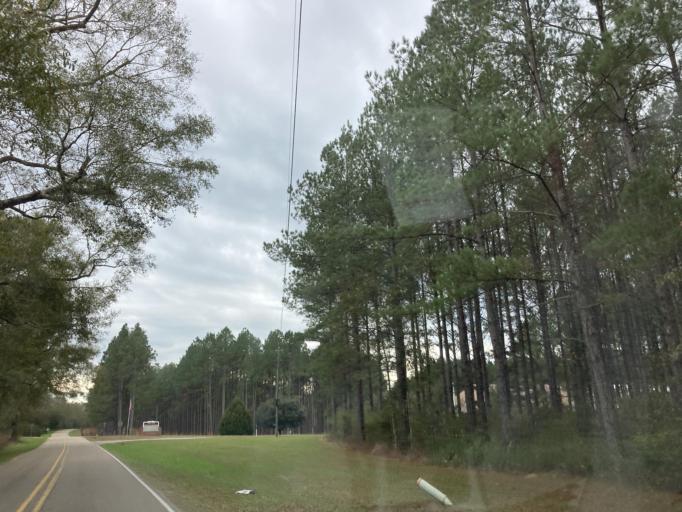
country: US
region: Mississippi
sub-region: Stone County
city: Wiggins
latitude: 30.9632
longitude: -89.2682
